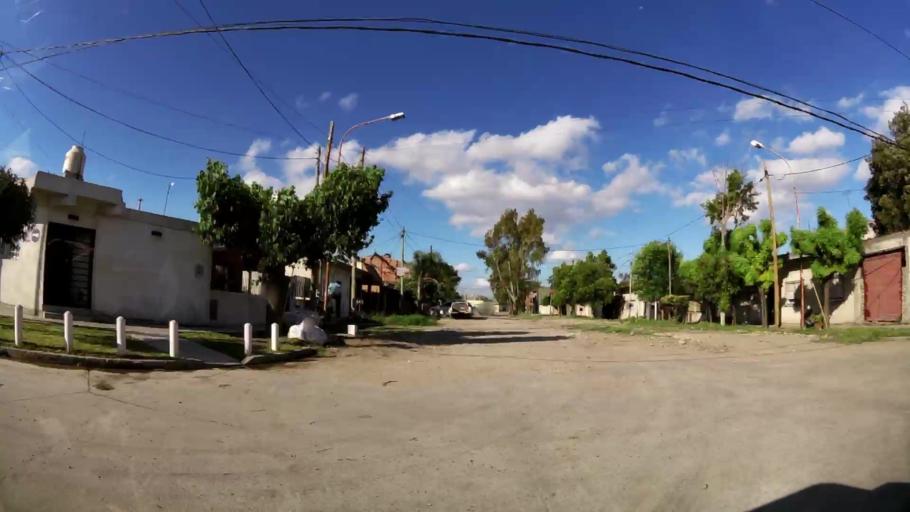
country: AR
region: Buenos Aires
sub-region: Partido de Moron
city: Moron
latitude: -34.6839
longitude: -58.6047
